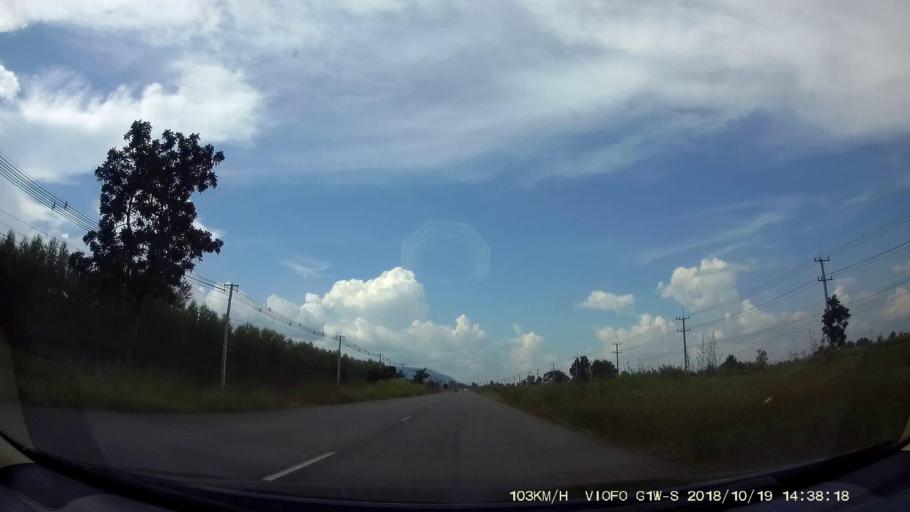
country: TH
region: Chaiyaphum
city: Kaeng Khro
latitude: 16.2111
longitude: 102.2026
